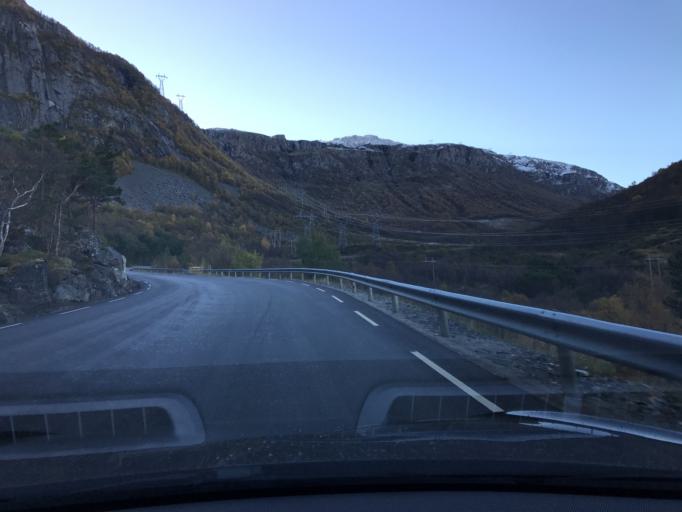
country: NO
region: Sogn og Fjordane
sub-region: Aurland
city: Aurlandsvangen
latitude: 60.8553
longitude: 7.3133
